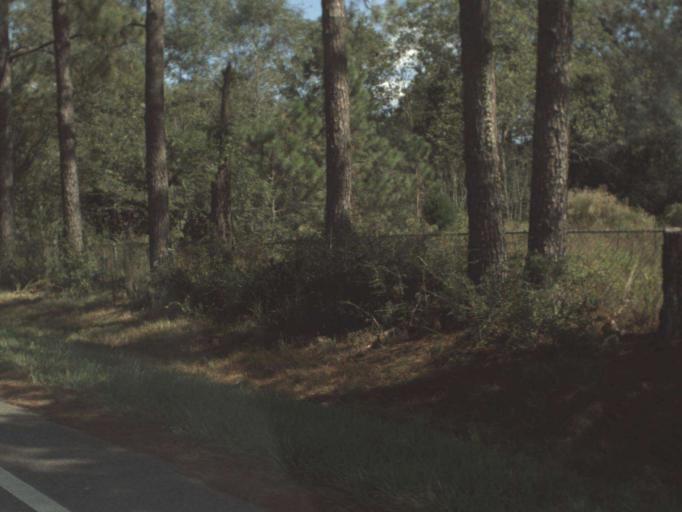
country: US
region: Alabama
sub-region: Geneva County
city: Samson
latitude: 30.9356
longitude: -86.1374
